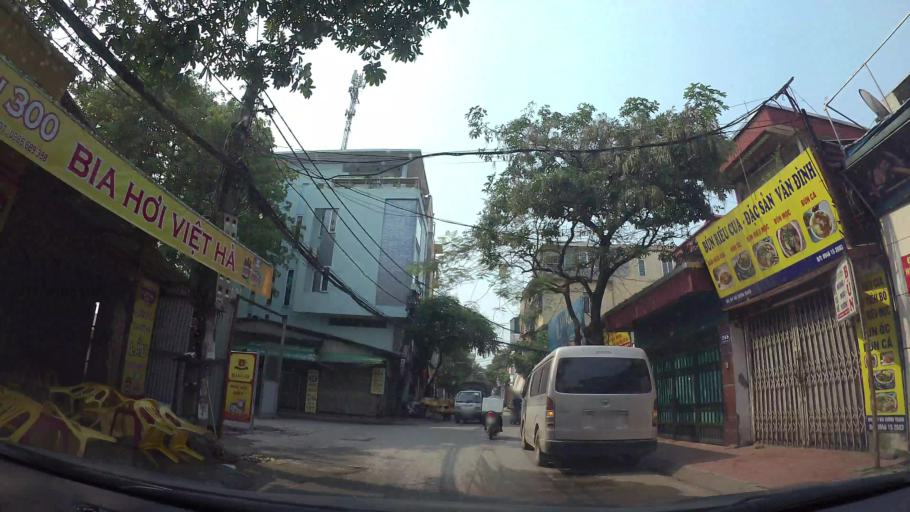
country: VN
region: Ha Noi
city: Thanh Xuan
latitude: 20.9862
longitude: 105.8191
